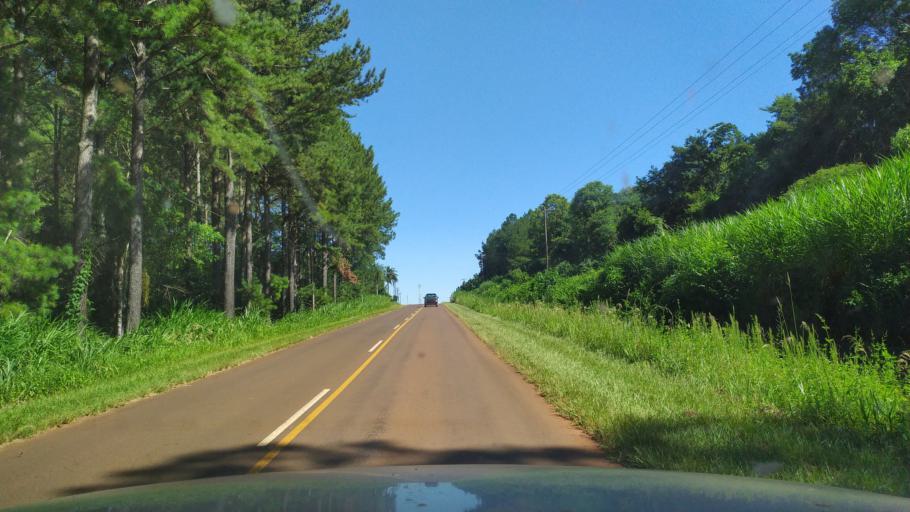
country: AR
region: Misiones
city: Caraguatay
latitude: -26.6634
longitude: -54.7327
